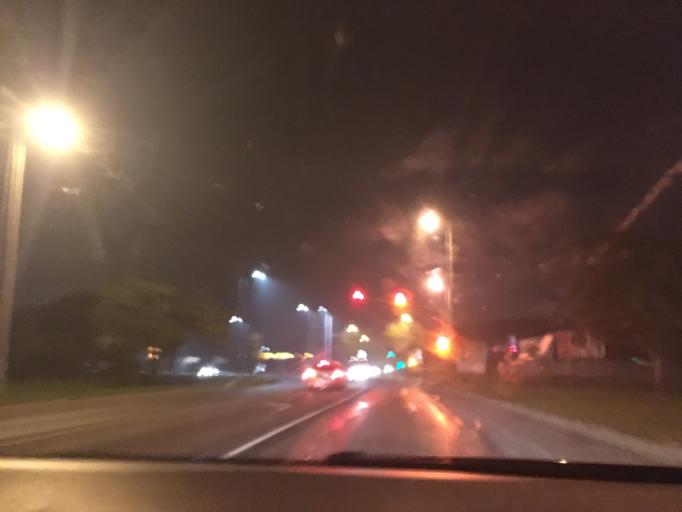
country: HU
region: Hajdu-Bihar
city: Debrecen
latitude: 47.5139
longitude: 21.6051
